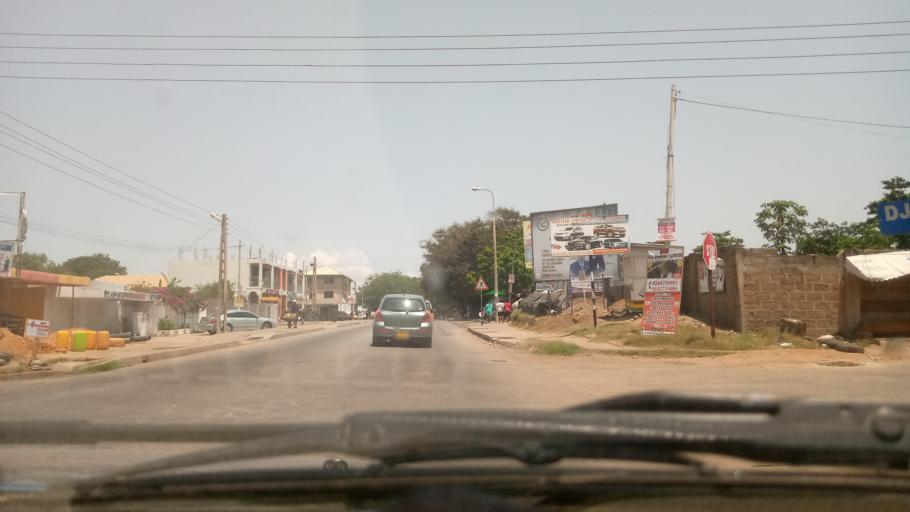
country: GH
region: Greater Accra
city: Accra
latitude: 5.5405
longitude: -0.2391
